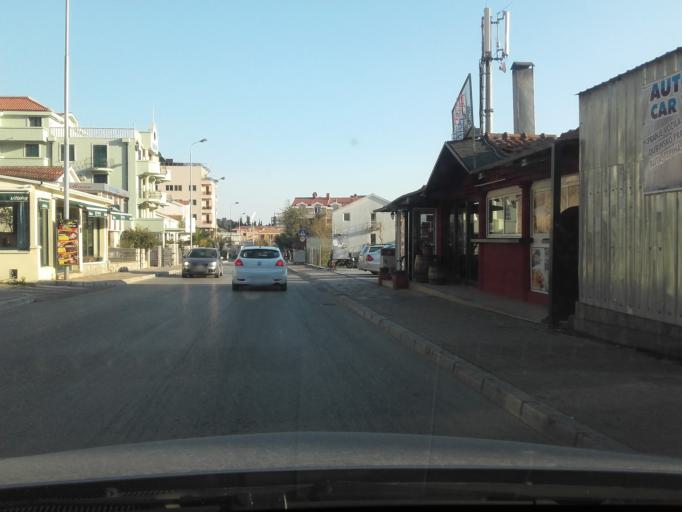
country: ME
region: Budva
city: Budva
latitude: 42.2901
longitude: 18.8509
